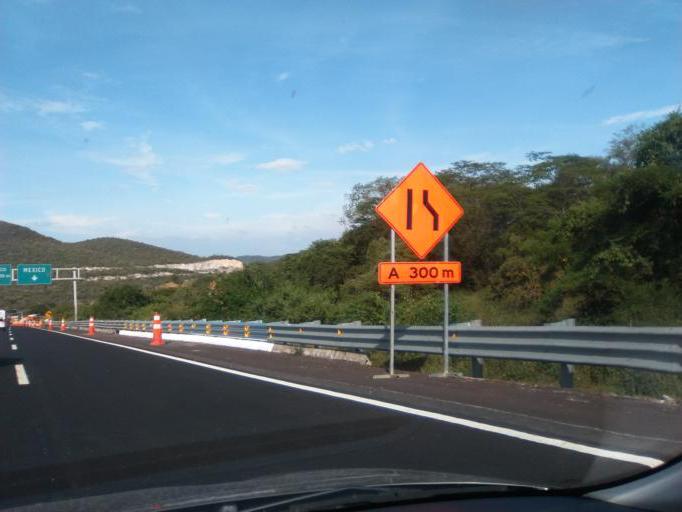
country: MX
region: Morelos
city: Tilzapotla
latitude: 18.4345
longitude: -99.1769
